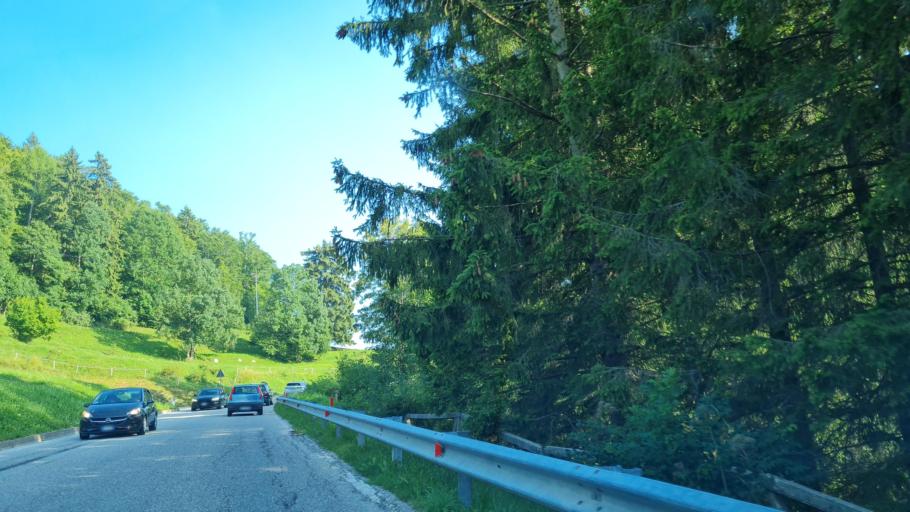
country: IT
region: Trentino-Alto Adige
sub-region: Provincia di Trento
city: Gionghi-Cappella
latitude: 45.9407
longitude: 11.2805
